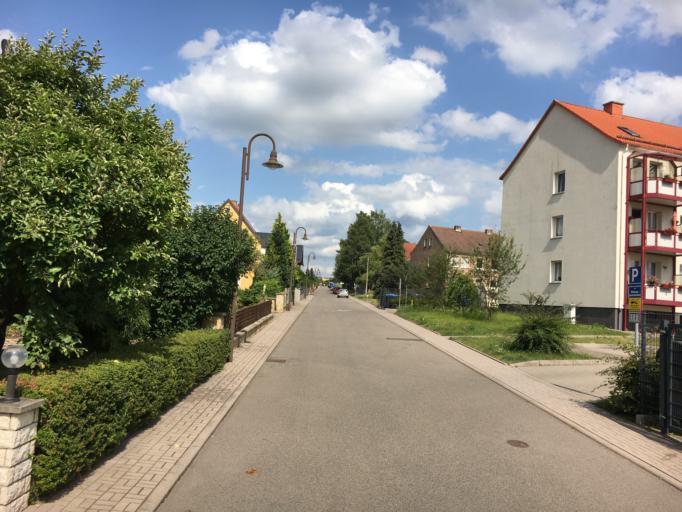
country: DE
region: Thuringia
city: Breitungen
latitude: 50.7640
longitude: 10.3316
